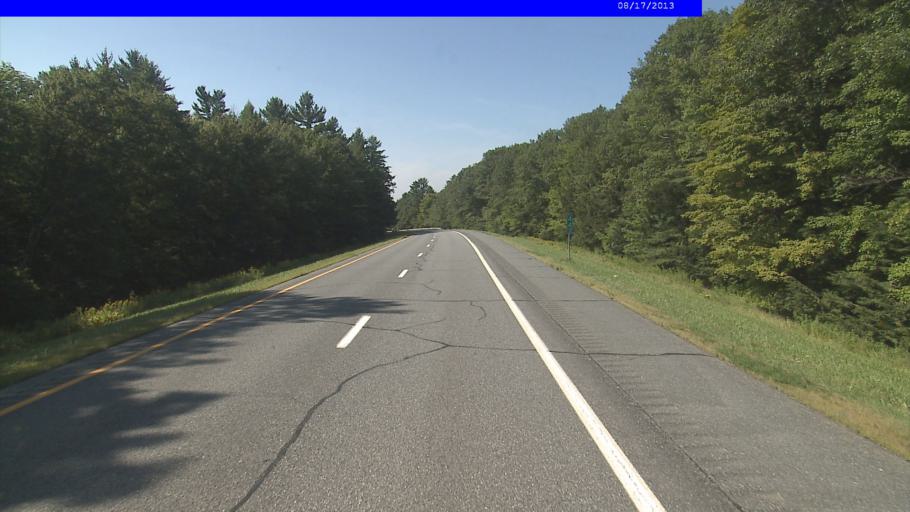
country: US
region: Vermont
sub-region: Windsor County
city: Springfield
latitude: 43.3022
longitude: -72.4257
